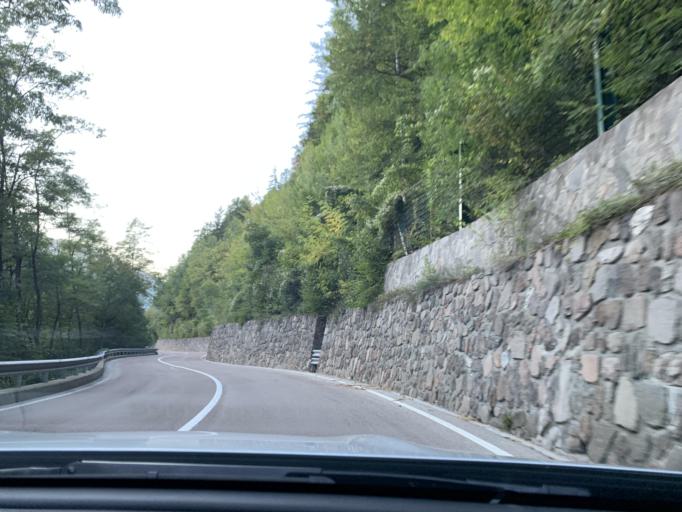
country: IT
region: Trentino-Alto Adige
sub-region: Bolzano
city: Nova Ponente
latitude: 46.4442
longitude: 11.4611
